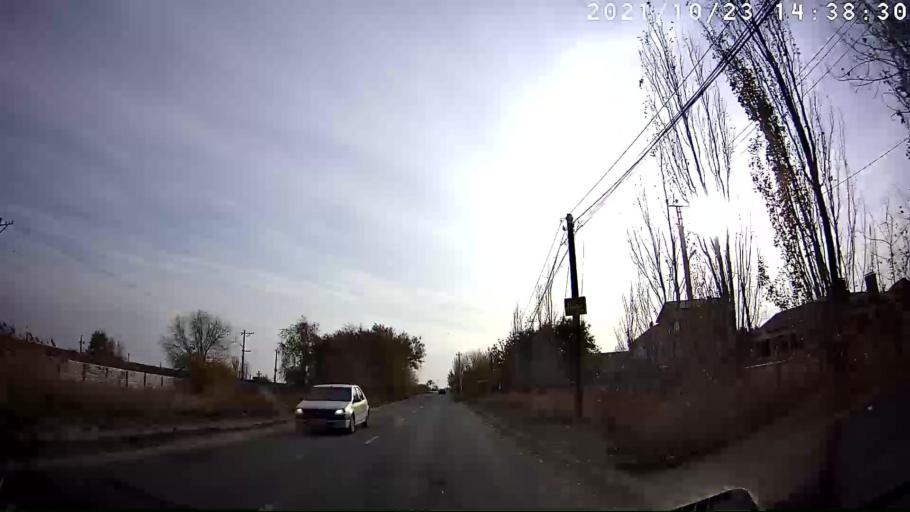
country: RU
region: Volgograd
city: Krasnoslobodsk
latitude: 48.4912
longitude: 44.5492
